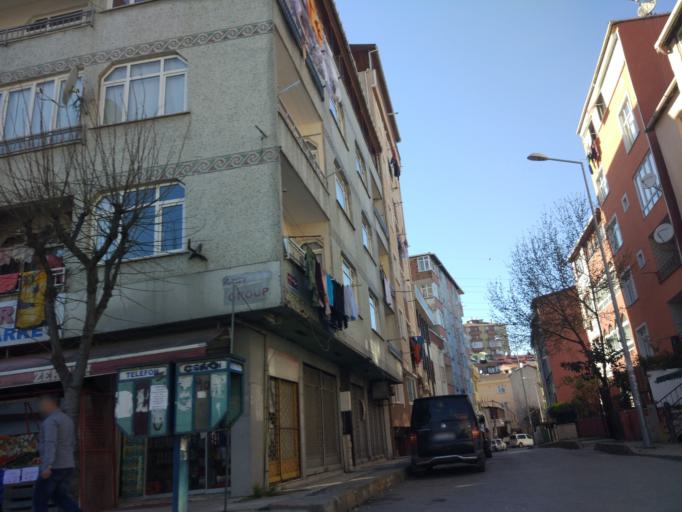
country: TR
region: Istanbul
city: Mahmutbey
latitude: 41.0193
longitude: 28.8050
